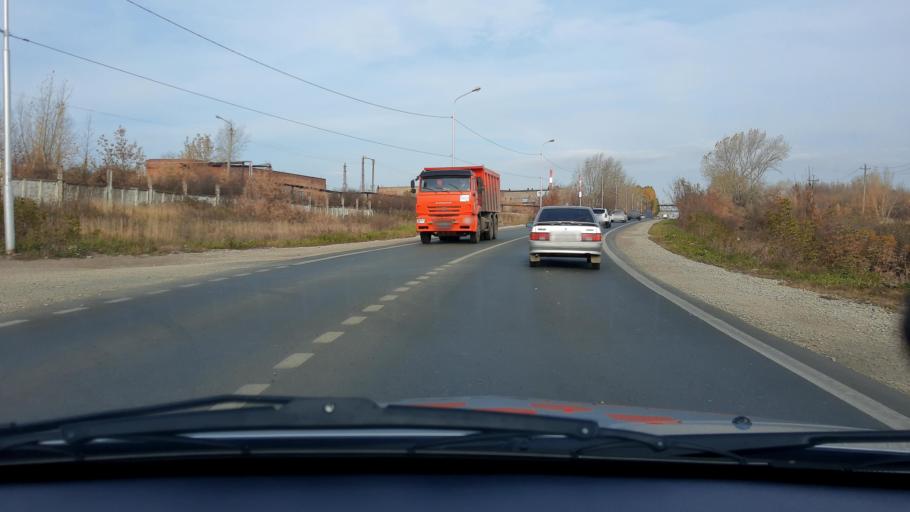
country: RU
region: Bashkortostan
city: Ufa
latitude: 54.8402
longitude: 56.1241
